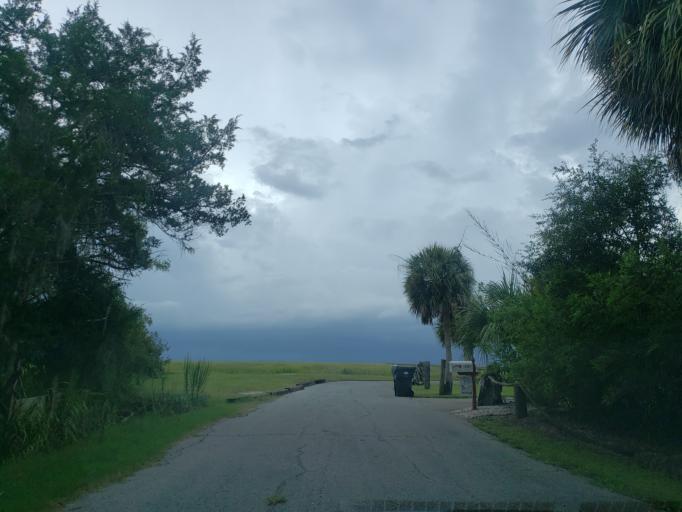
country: US
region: Georgia
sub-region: Chatham County
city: Wilmington Island
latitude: 32.0039
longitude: -80.9611
